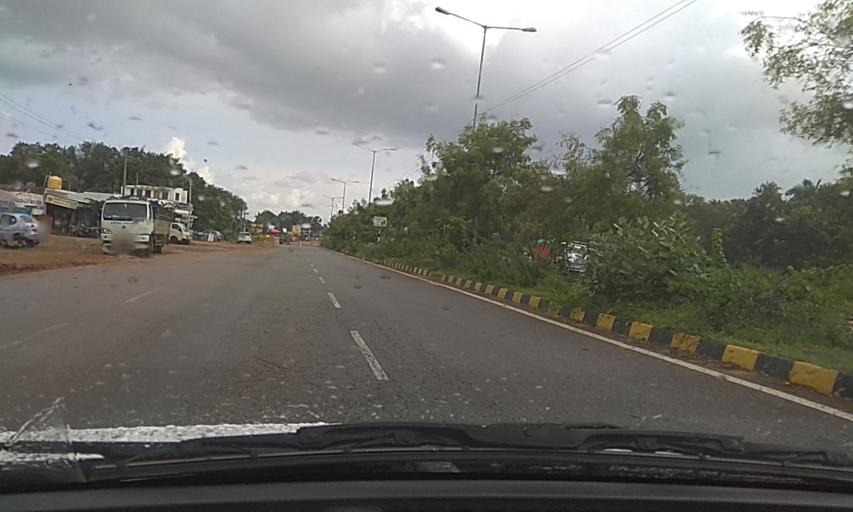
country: IN
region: Karnataka
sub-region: Mysore
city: Mysore
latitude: 12.2985
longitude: 76.7051
